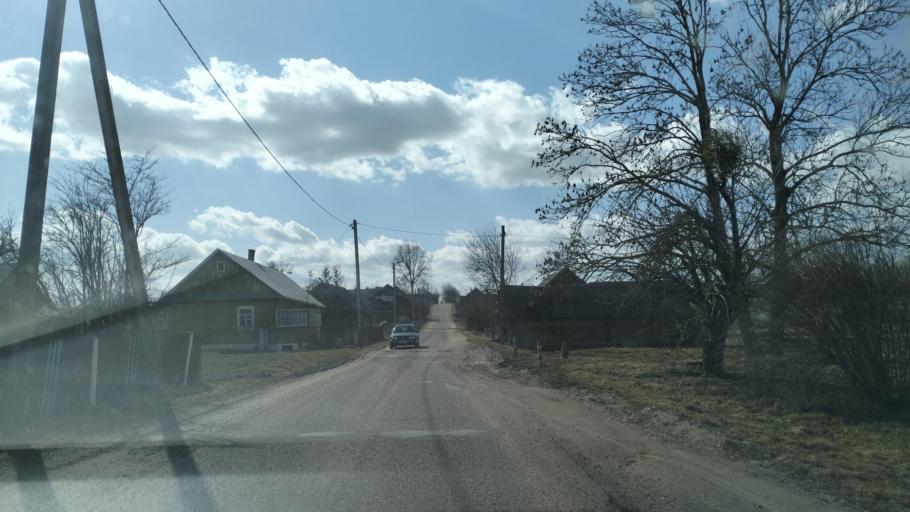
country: BY
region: Grodnenskaya
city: Karelichy
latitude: 53.6585
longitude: 26.1079
